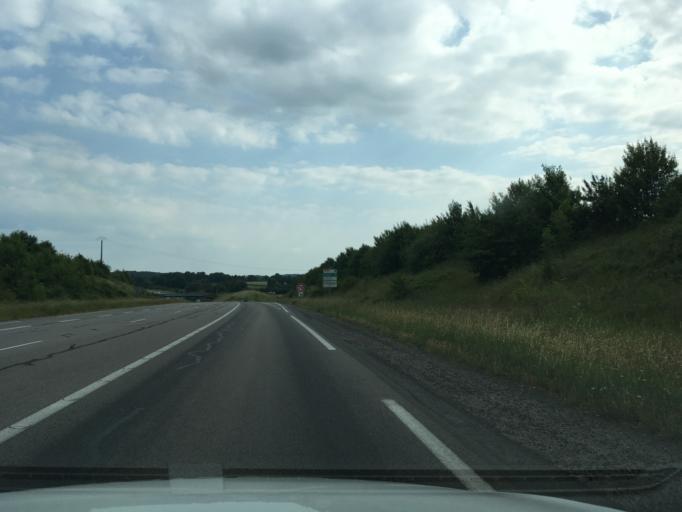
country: FR
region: Poitou-Charentes
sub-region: Departement des Deux-Sevres
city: Le Tallud
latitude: 46.6426
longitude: -0.2762
